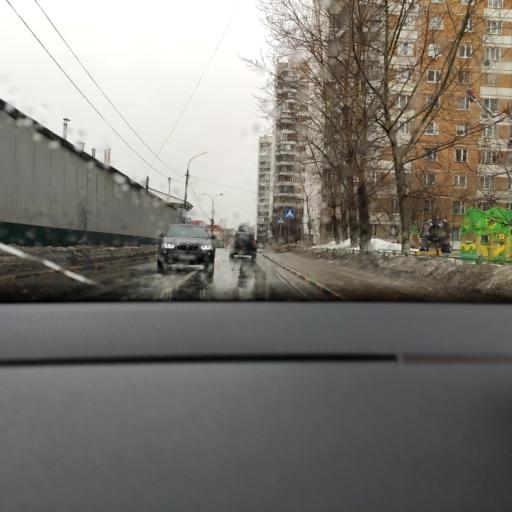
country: RU
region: Moskovskaya
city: Oktyabr'skiy
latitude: 55.6087
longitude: 37.9680
